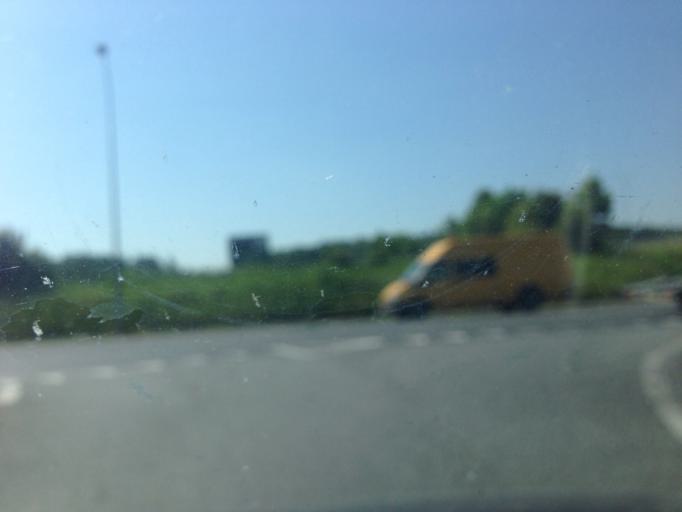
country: PL
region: Pomeranian Voivodeship
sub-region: Powiat tczewski
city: Pelplin
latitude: 53.9278
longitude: 18.6422
